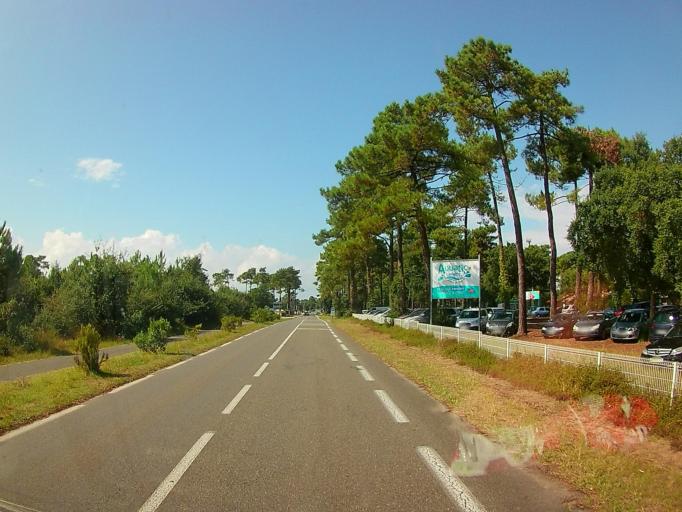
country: FR
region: Aquitaine
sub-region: Departement des Landes
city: Labenne
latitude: 43.5940
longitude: -1.4532
